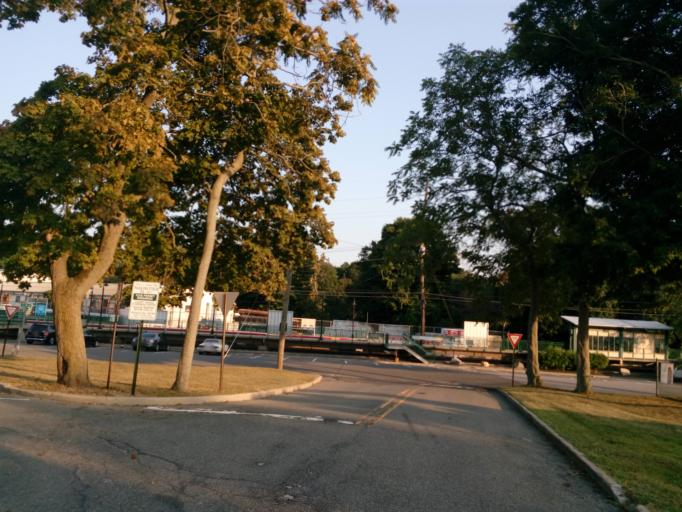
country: US
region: New York
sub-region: Nassau County
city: Locust Valley
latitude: 40.8744
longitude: -73.5995
